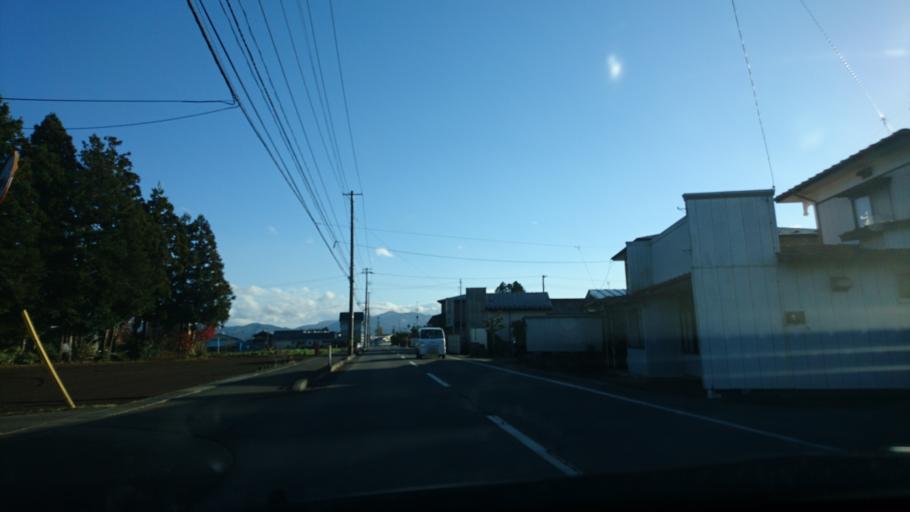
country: JP
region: Iwate
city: Mizusawa
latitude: 39.1110
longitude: 141.1556
